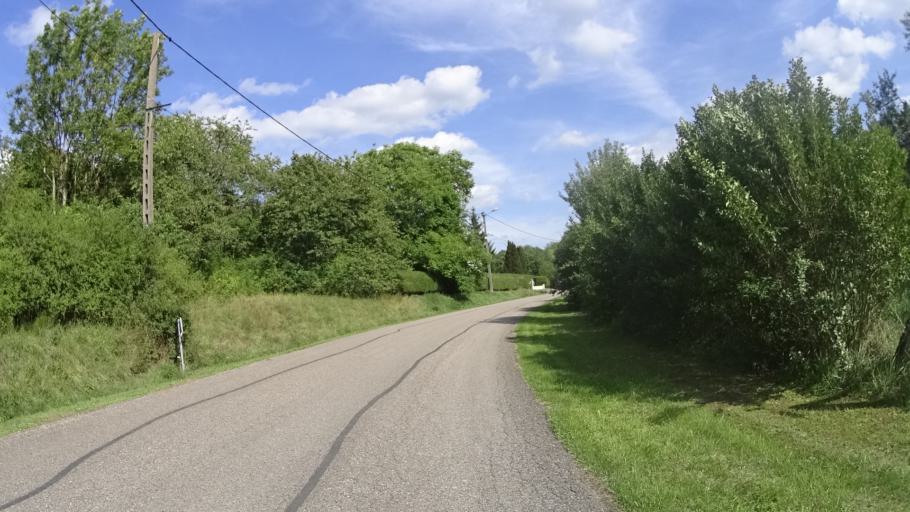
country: FR
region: Lorraine
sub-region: Departement de Meurthe-et-Moselle
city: Dommartin-les-Toul
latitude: 48.6495
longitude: 5.9092
